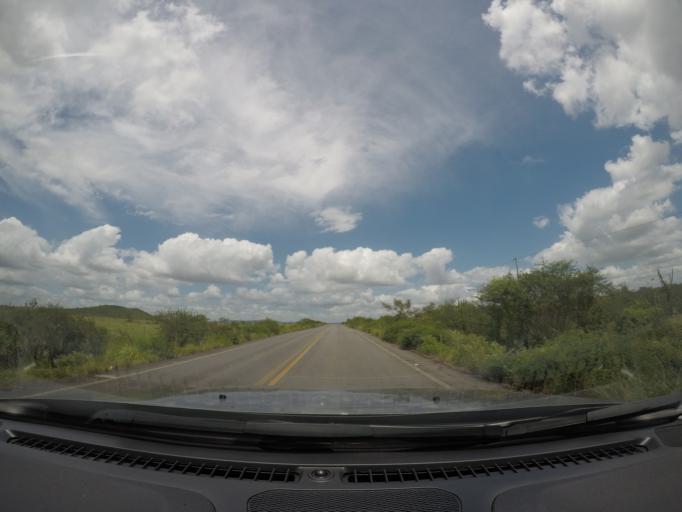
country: BR
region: Bahia
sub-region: Ipira
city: Ipira
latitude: -12.2397
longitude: -39.7998
